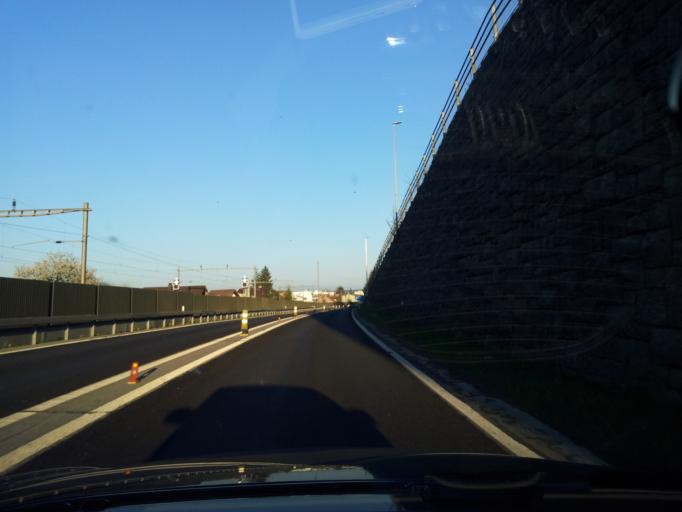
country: CH
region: Bern
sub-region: Biel/Bienne District
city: Brugg
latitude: 47.1176
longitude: 7.2902
